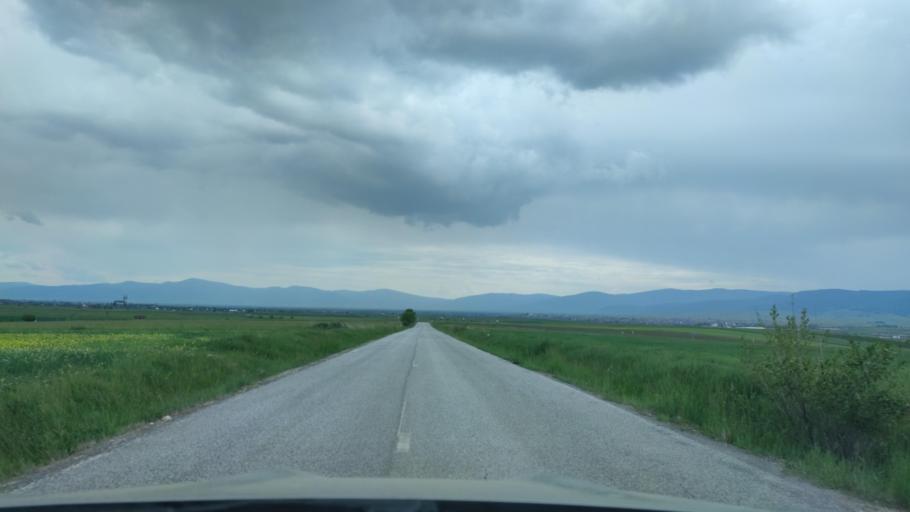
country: RO
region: Harghita
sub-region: Comuna Ditrau
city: Ditrau
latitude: 46.8355
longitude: 25.4943
